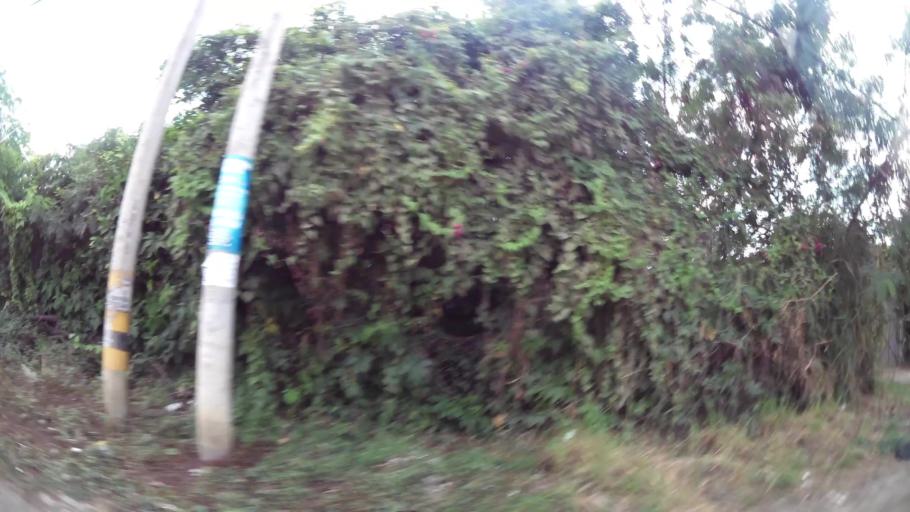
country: CO
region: Valle del Cauca
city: Cali
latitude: 3.4466
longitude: -76.4717
